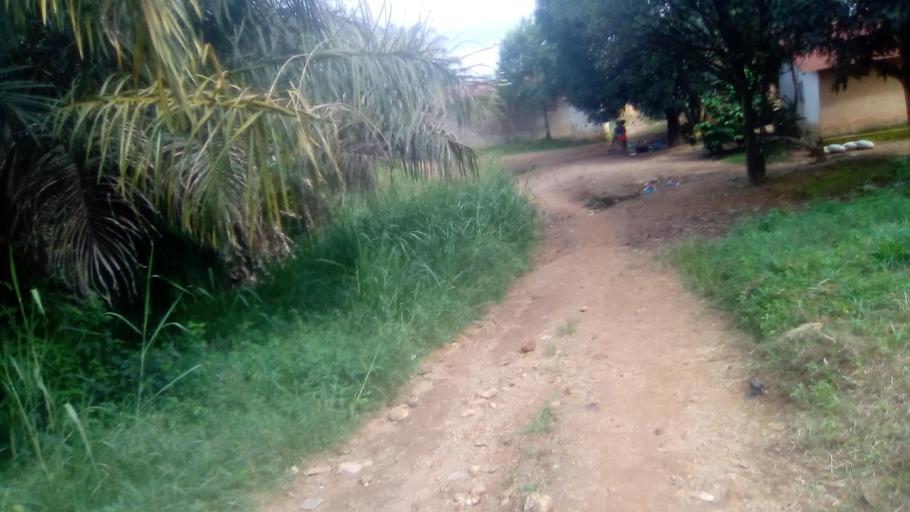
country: SL
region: Eastern Province
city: Kailahun
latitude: 8.2854
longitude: -10.5620
